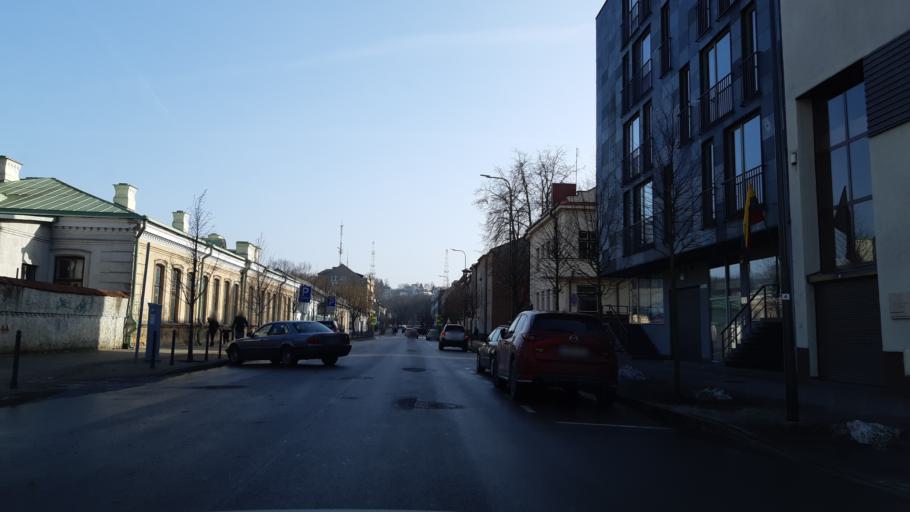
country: LT
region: Kauno apskritis
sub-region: Kaunas
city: Kaunas
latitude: 54.8938
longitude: 23.9187
